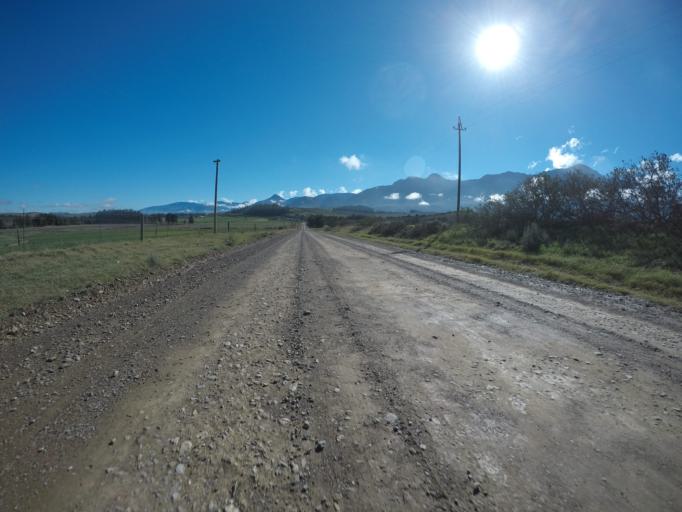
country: ZA
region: Western Cape
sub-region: Overberg District Municipality
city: Caledon
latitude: -34.1027
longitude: 19.7023
